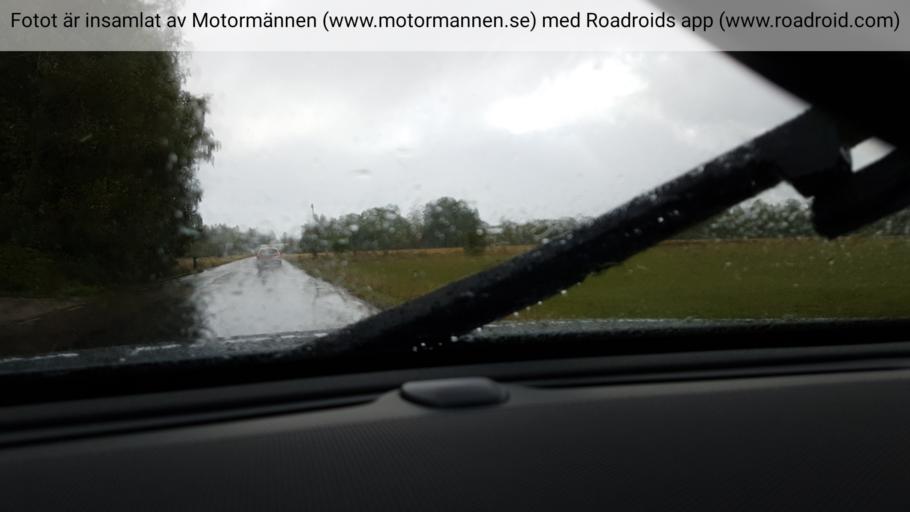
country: SE
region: Vaestra Goetaland
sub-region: Vanersborgs Kommun
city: Vanersborg
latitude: 58.3610
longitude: 12.2681
